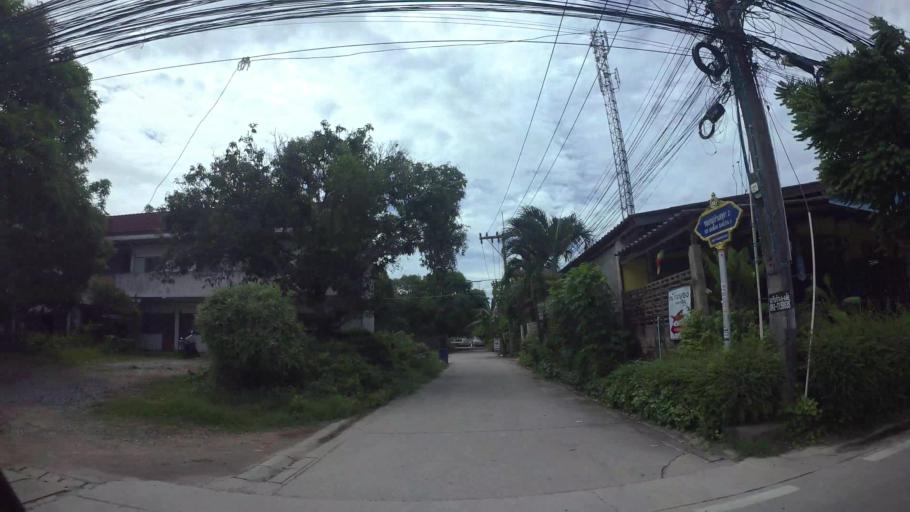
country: TH
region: Rayong
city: Rayong
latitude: 12.6698
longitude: 101.2831
